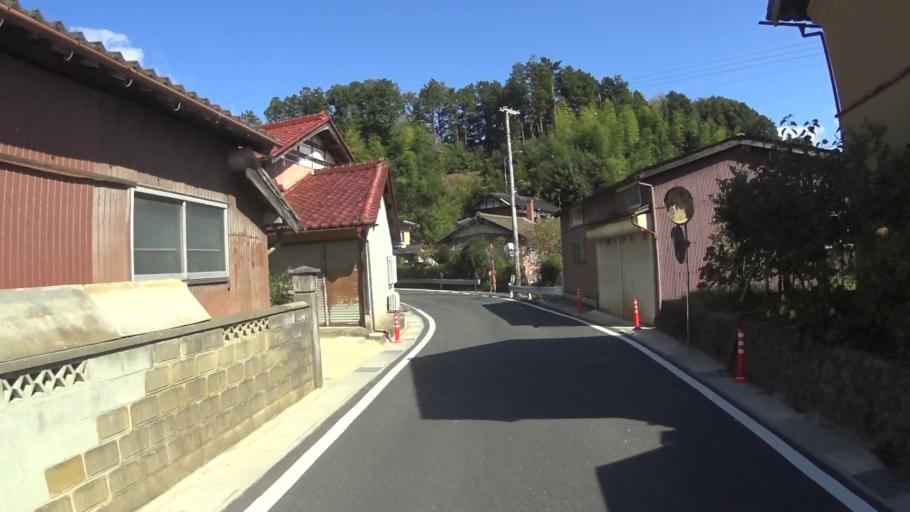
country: JP
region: Kyoto
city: Miyazu
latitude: 35.6327
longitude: 135.0724
